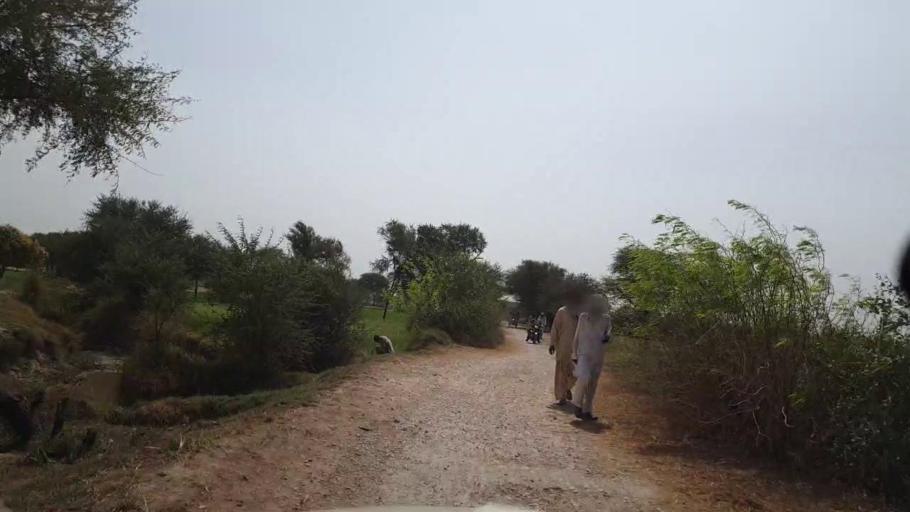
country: PK
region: Sindh
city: Matli
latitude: 25.0440
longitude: 68.6976
